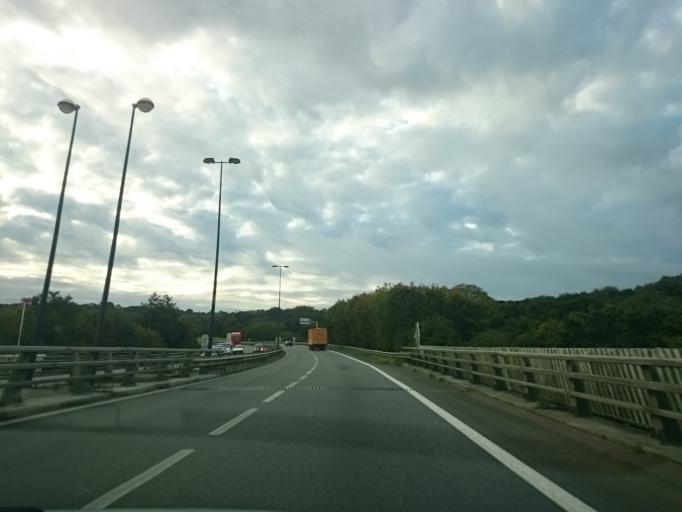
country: FR
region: Brittany
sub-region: Departement du Finistere
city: Le Relecq-Kerhuon
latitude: 48.3855
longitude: -4.3957
